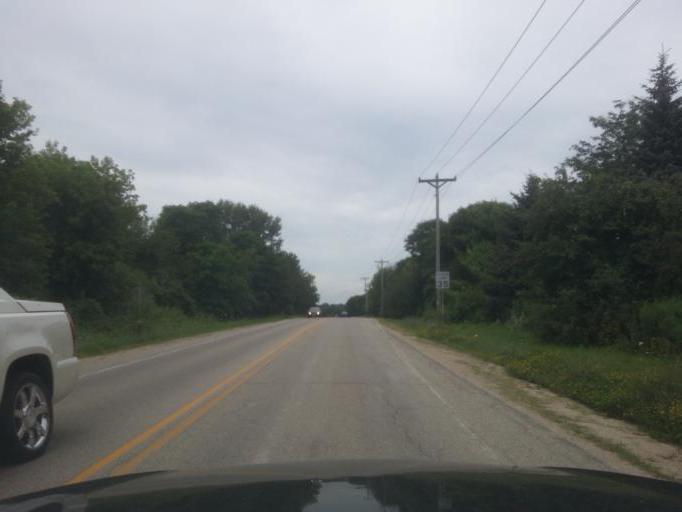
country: US
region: Wisconsin
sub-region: Dane County
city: Monona
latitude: 43.0752
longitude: -89.2738
